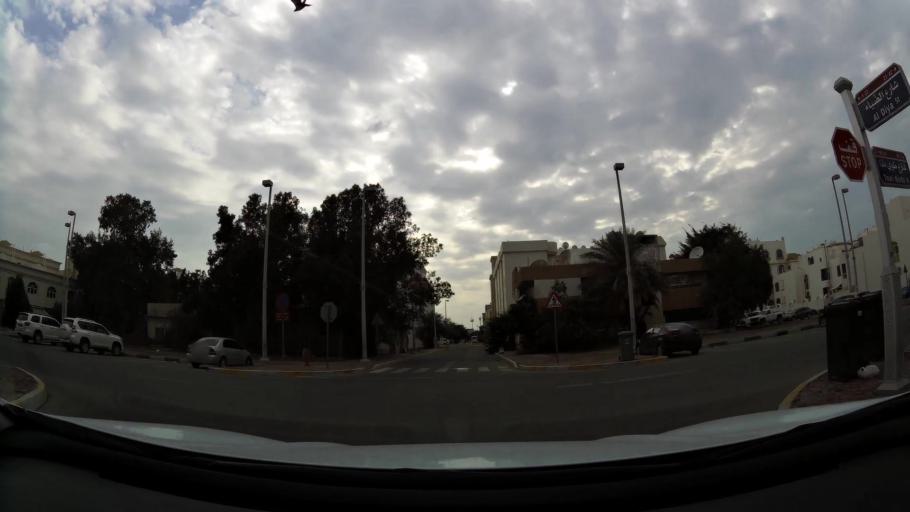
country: AE
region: Abu Dhabi
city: Abu Dhabi
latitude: 24.4454
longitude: 54.3981
